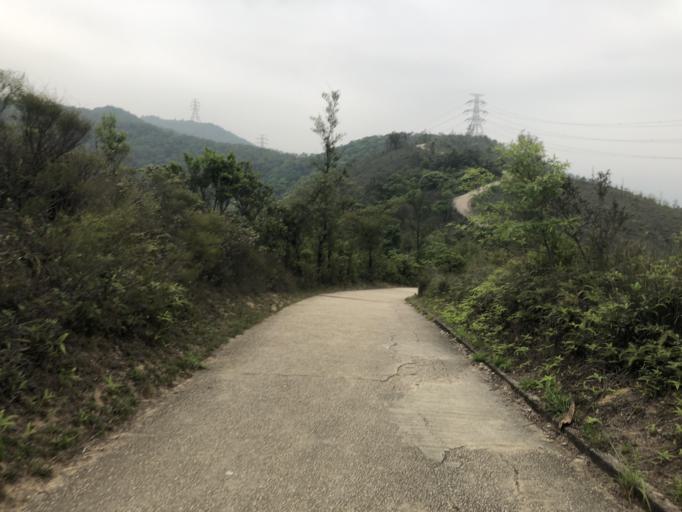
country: HK
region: Sha Tin
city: Sha Tin
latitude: 22.3915
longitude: 114.1633
